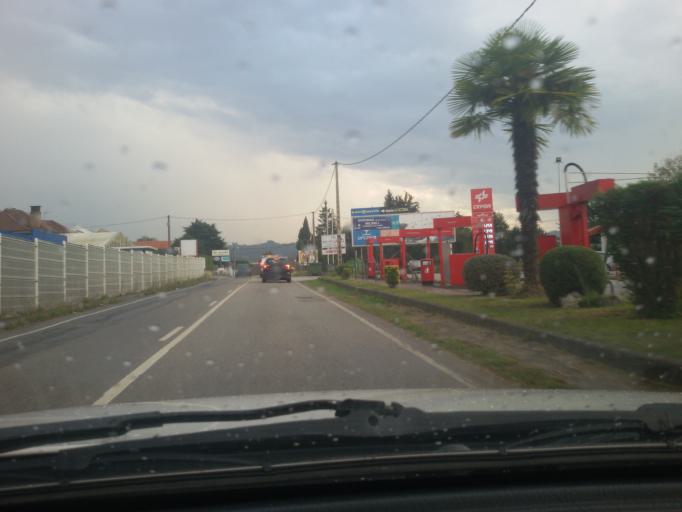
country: ES
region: Asturias
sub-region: Province of Asturias
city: Lugones
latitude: 43.3831
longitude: -5.7836
